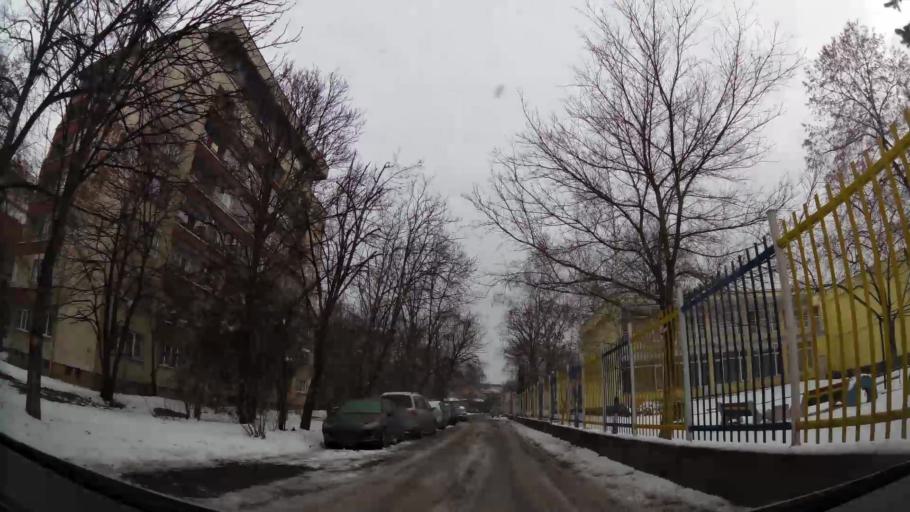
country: BG
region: Sofia-Capital
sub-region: Stolichna Obshtina
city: Sofia
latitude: 42.7161
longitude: 23.2903
